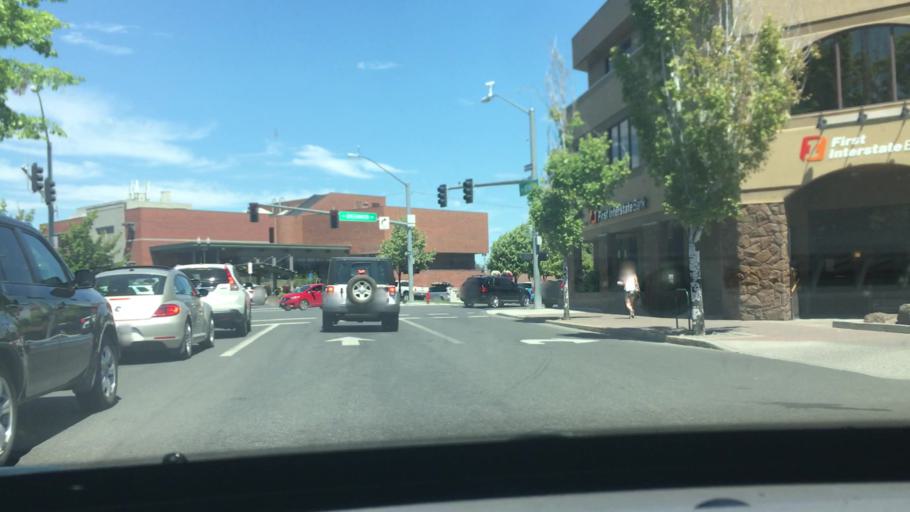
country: US
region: Oregon
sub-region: Deschutes County
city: Bend
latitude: 44.0596
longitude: -121.3116
